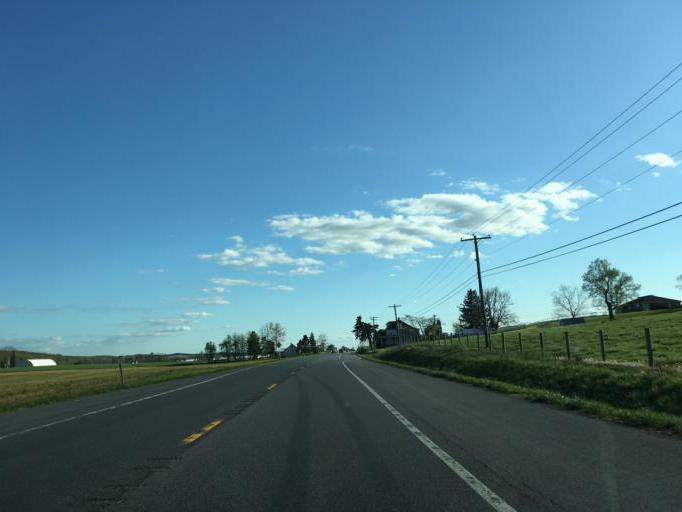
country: US
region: Maryland
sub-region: Frederick County
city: Woodsboro
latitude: 39.5156
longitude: -77.3187
